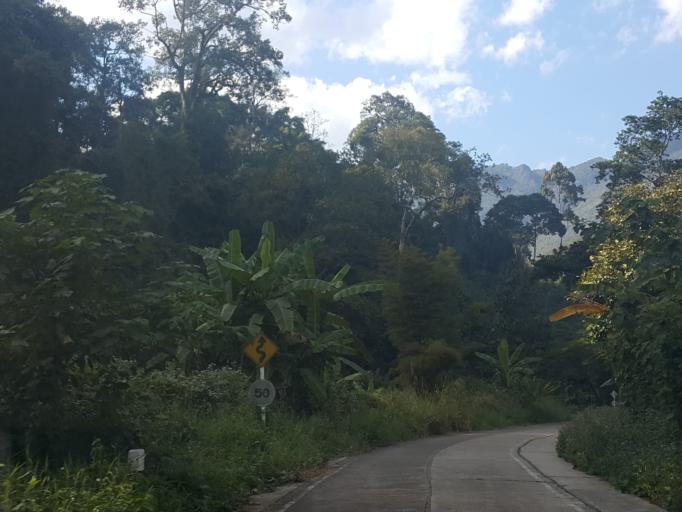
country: TH
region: Chiang Mai
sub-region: Amphoe Chiang Dao
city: Chiang Dao
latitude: 19.4102
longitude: 98.9226
